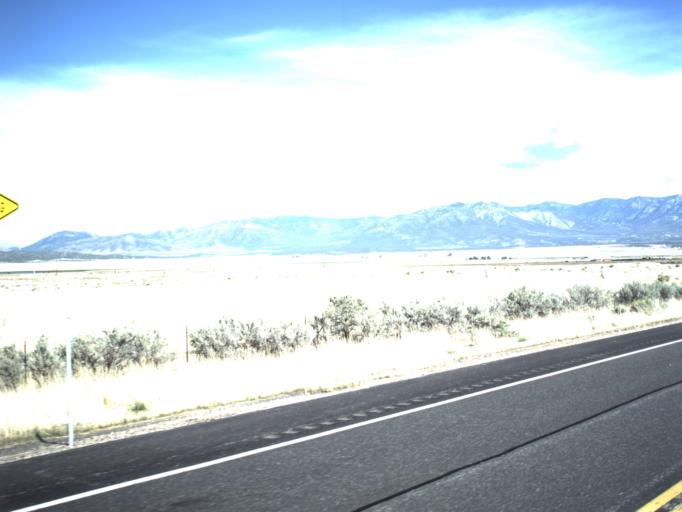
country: US
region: Utah
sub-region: Millard County
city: Fillmore
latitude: 39.1364
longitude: -112.3658
